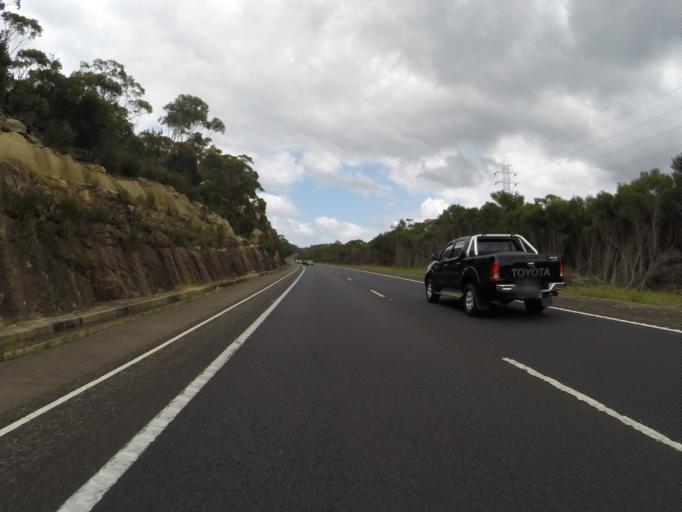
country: AU
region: New South Wales
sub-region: Wollongong
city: Helensburgh
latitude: -34.1916
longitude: 150.9670
